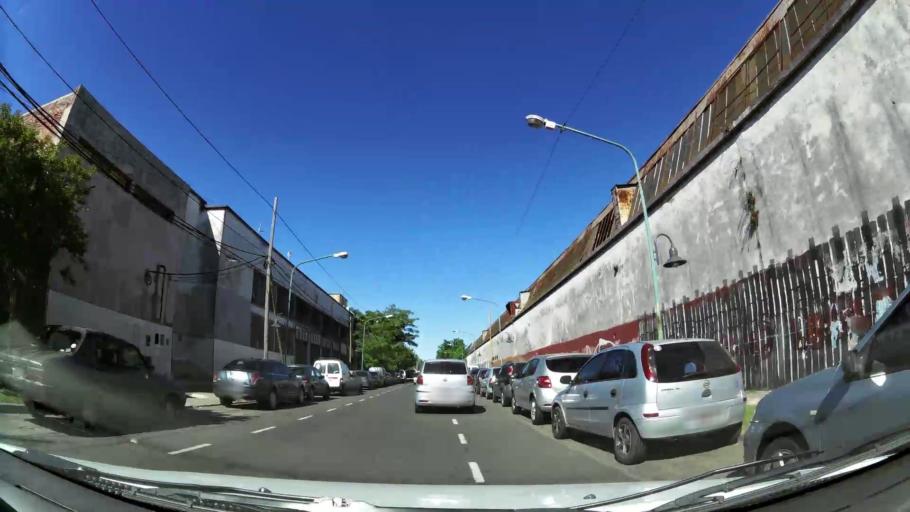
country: AR
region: Buenos Aires
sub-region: Partido de General San Martin
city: General San Martin
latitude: -34.5425
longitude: -58.5152
